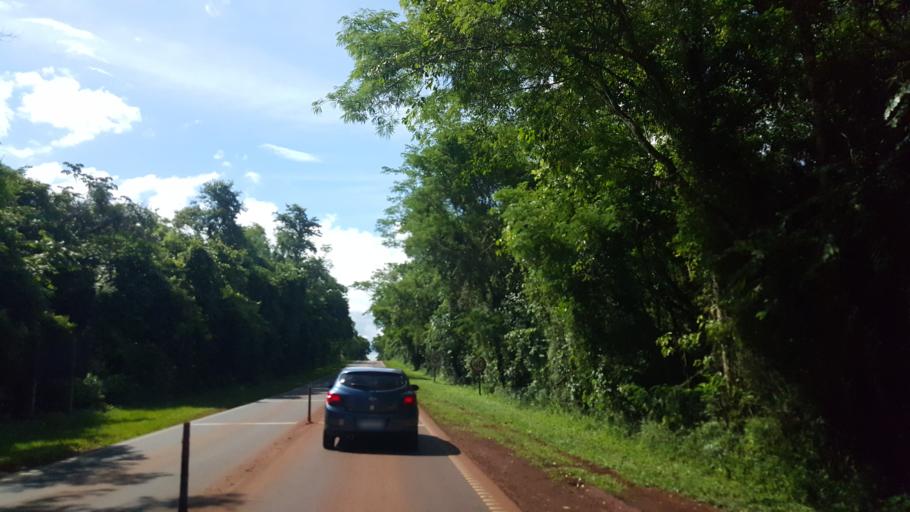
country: AR
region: Misiones
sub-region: Departamento de Iguazu
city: Puerto Iguazu
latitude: -25.6897
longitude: -54.4789
